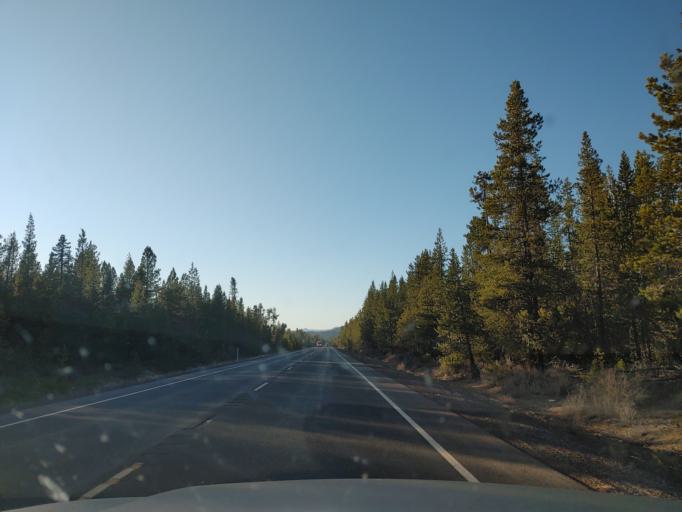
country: US
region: Oregon
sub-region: Deschutes County
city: La Pine
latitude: 43.3986
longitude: -121.8192
